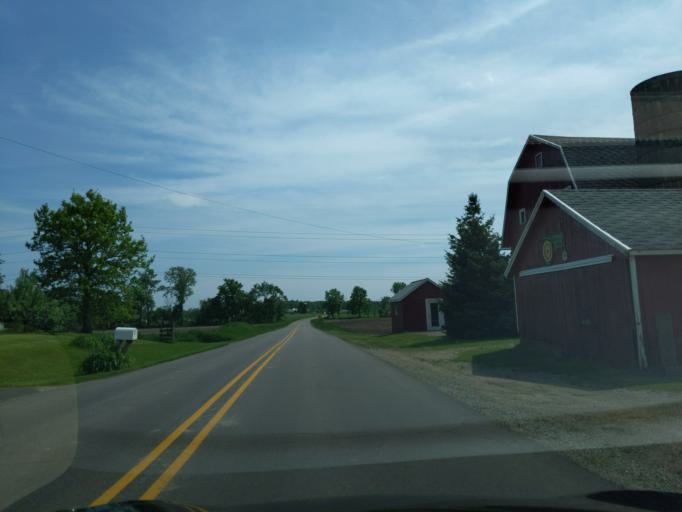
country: US
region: Michigan
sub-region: Ingham County
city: Leslie
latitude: 42.4194
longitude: -84.3124
